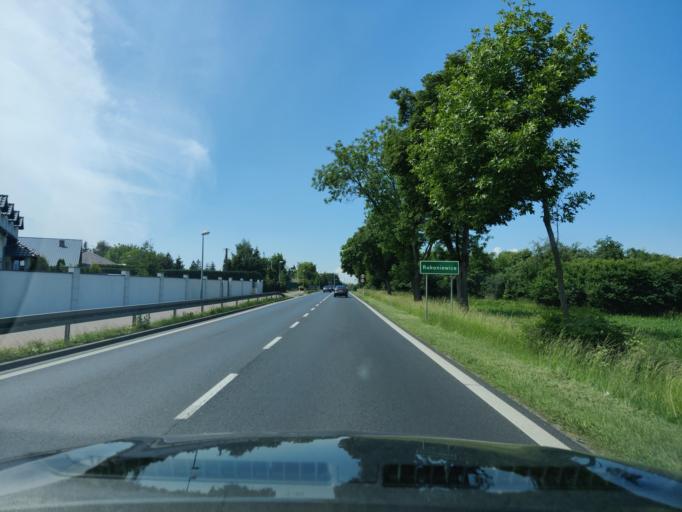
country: PL
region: Greater Poland Voivodeship
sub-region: Powiat grodziski
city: Rakoniewice
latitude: 52.1491
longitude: 16.2896
